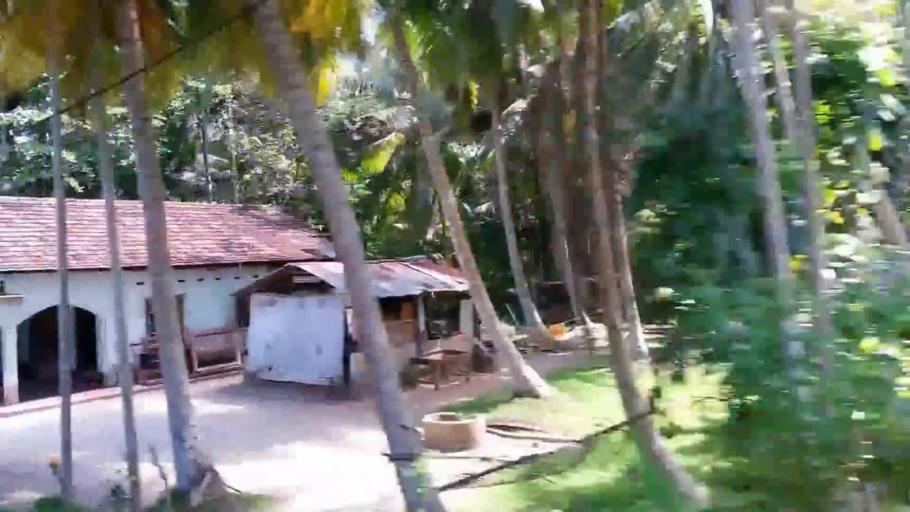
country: LK
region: Southern
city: Hikkaduwa
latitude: 6.1657
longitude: 80.0910
